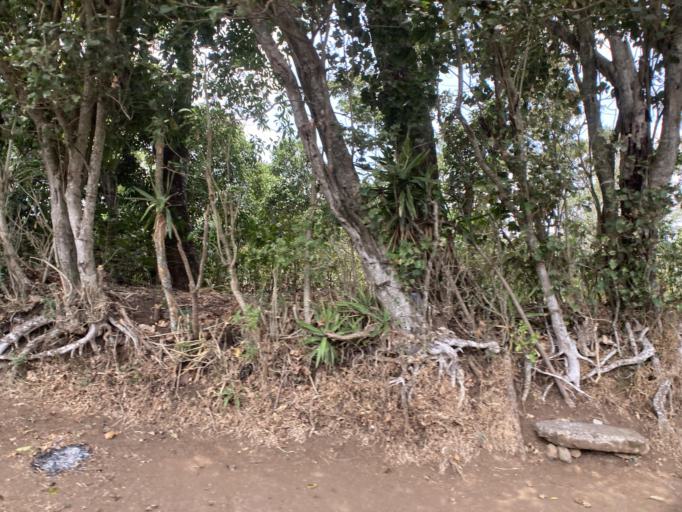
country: GT
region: Escuintla
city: San Vicente Pacaya
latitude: 14.3451
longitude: -90.5706
